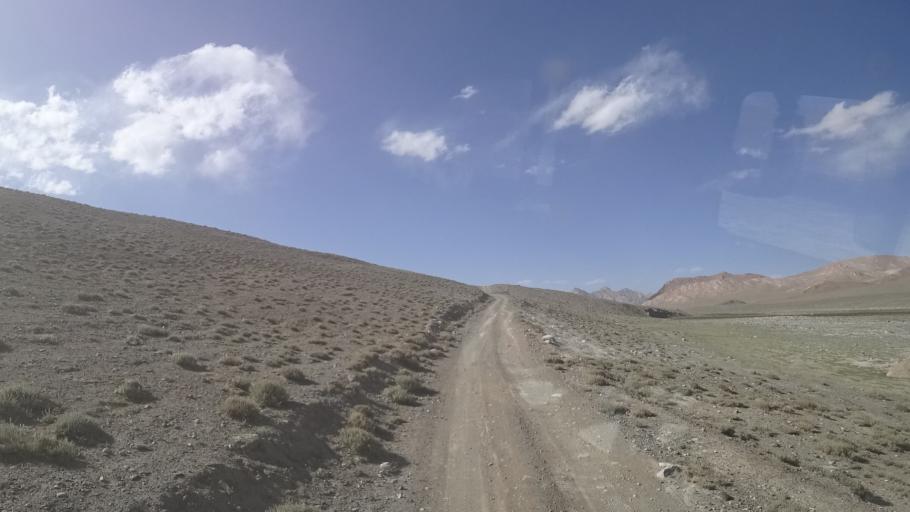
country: TJ
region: Gorno-Badakhshan
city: Murghob
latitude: 37.5757
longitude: 74.1572
